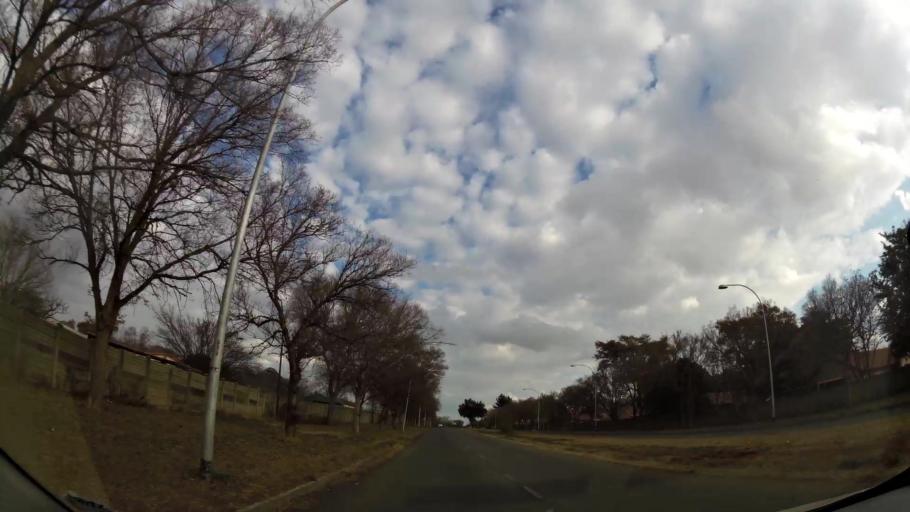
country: ZA
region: Orange Free State
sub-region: Fezile Dabi District Municipality
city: Sasolburg
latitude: -26.8123
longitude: 27.8094
